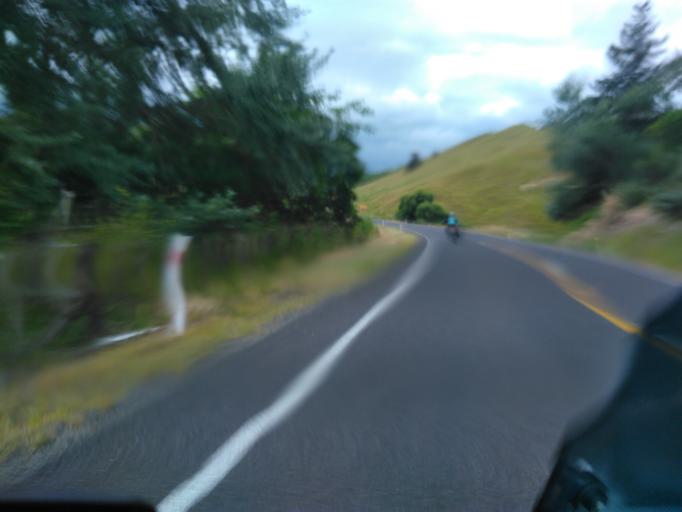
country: NZ
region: Gisborne
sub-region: Gisborne District
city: Gisborne
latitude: -38.4772
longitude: 177.8582
